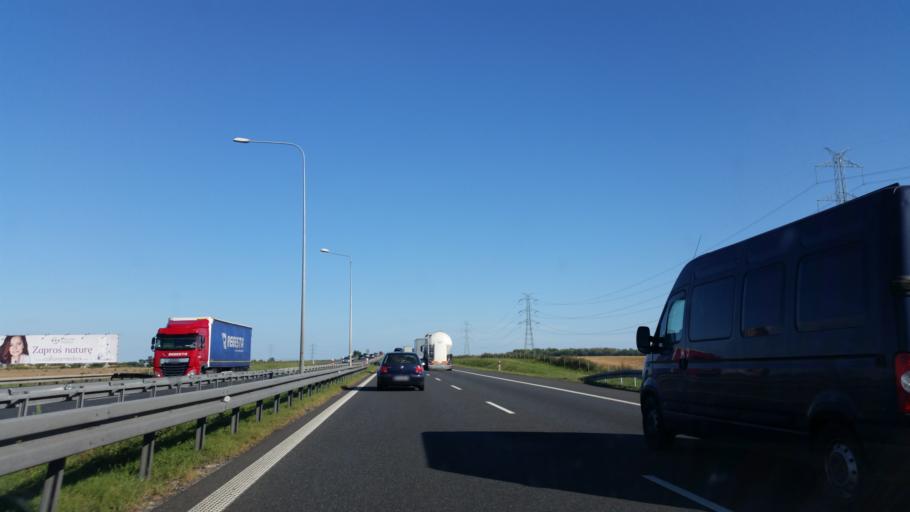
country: PL
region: Opole Voivodeship
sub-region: Powiat brzeski
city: Olszanka
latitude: 50.7530
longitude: 17.4374
